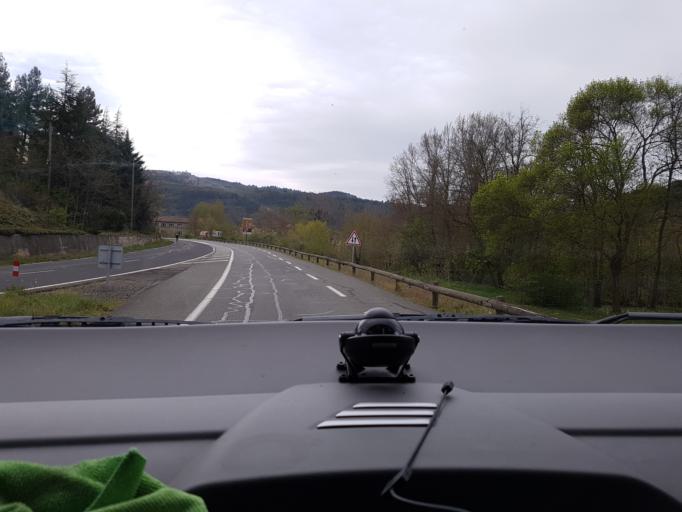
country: FR
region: Languedoc-Roussillon
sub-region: Departement de l'Aude
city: Couiza
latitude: 42.9482
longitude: 2.2533
